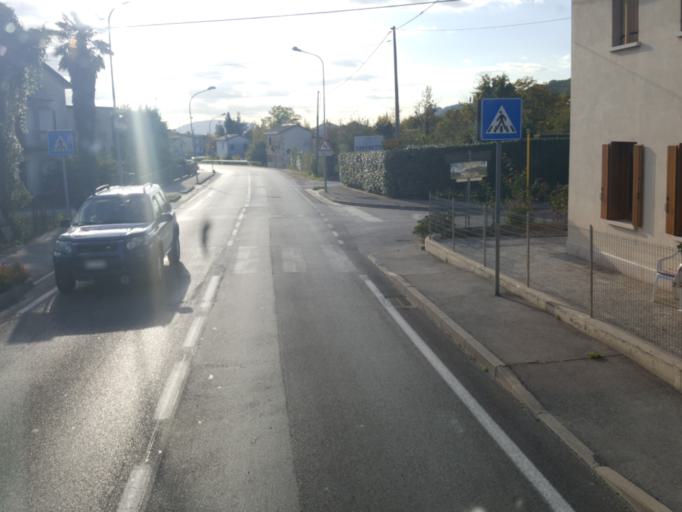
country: IT
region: Veneto
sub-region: Provincia di Treviso
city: Col San Martino
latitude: 45.9022
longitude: 12.1146
